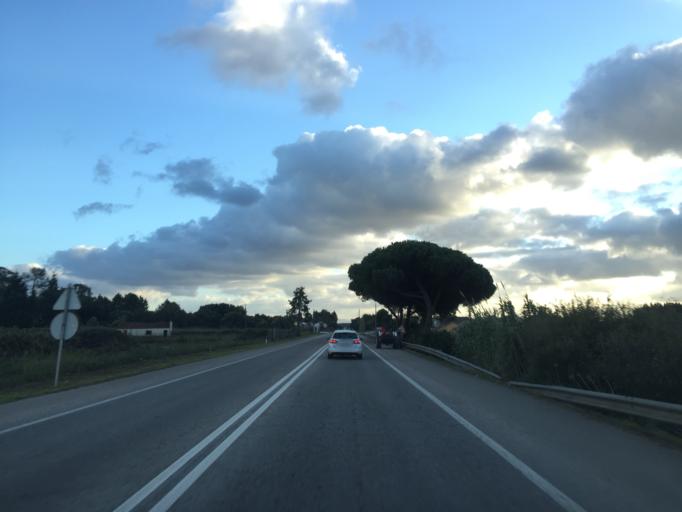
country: PT
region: Leiria
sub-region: Alcobaca
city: Benedita
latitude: 39.4453
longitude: -8.9519
